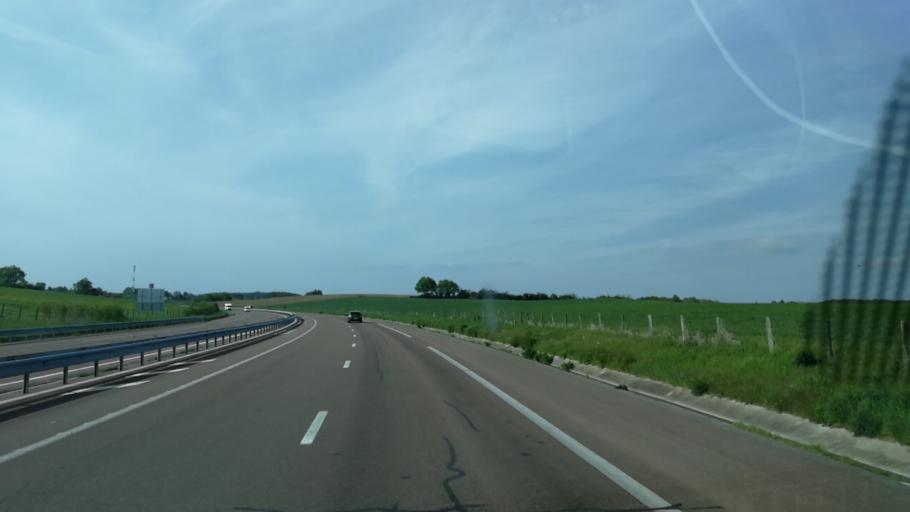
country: FR
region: Bourgogne
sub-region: Departement de la Nievre
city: Magny-Cours
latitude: 46.8843
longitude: 3.1609
